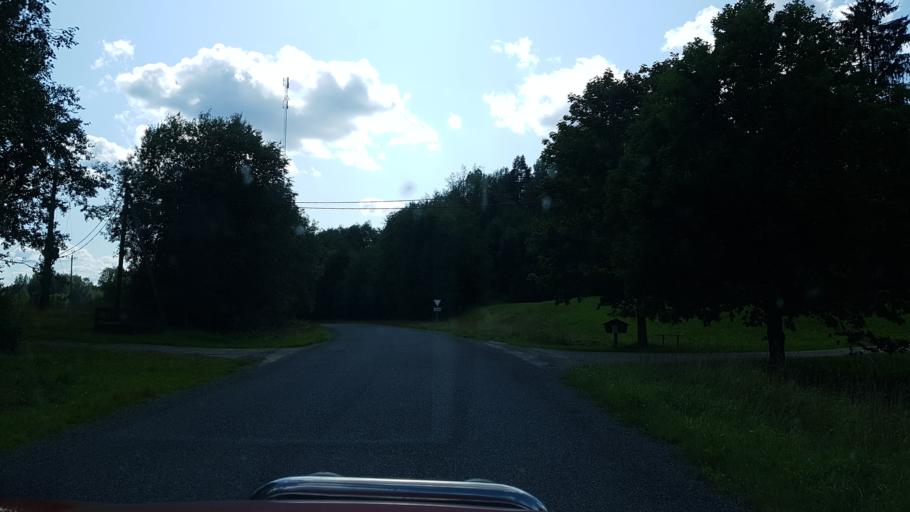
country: LV
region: Aluksnes Rajons
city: Aluksne
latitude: 57.5948
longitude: 27.0865
